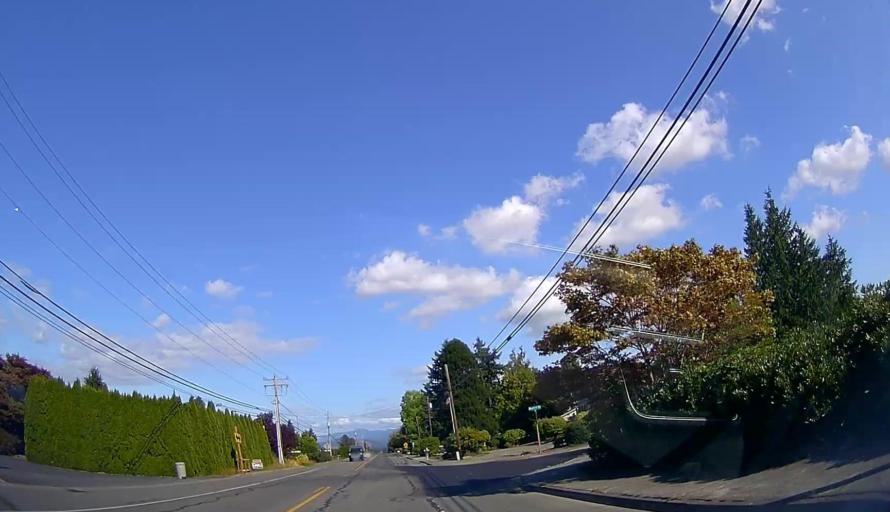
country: US
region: Washington
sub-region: Skagit County
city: Burlington
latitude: 48.4721
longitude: -122.3854
